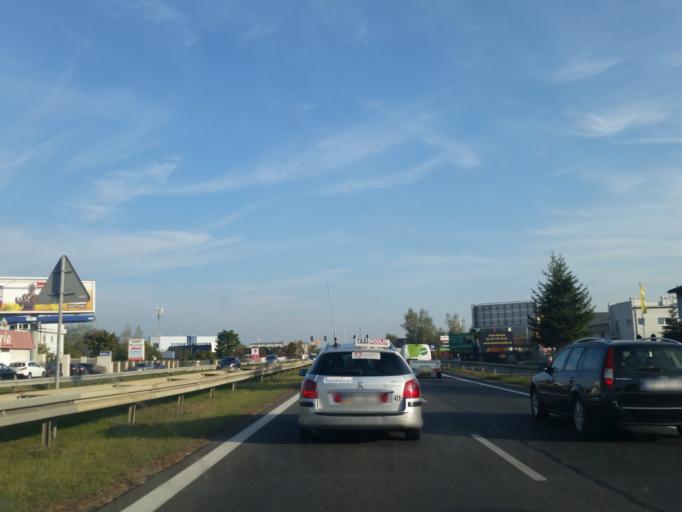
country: PL
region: Masovian Voivodeship
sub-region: Powiat warszawski zachodni
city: Lomianki
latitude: 52.3394
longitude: 20.8710
